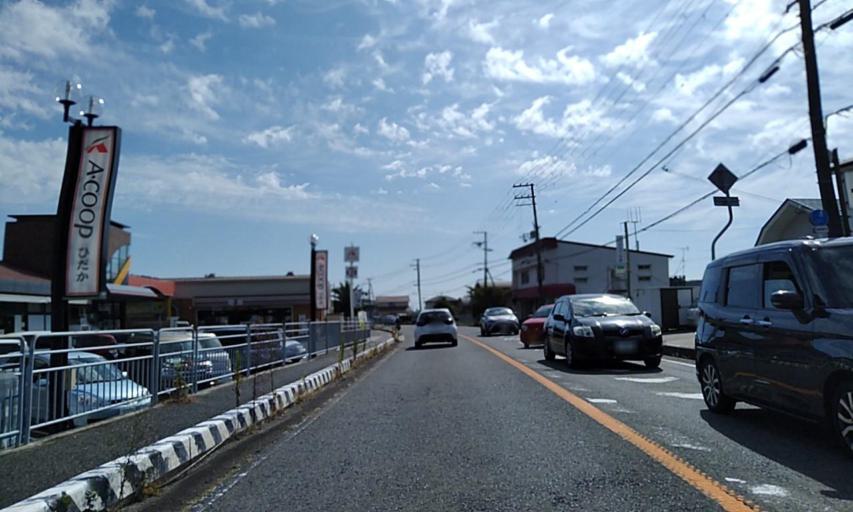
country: JP
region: Wakayama
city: Gobo
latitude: 33.9248
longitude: 135.1440
